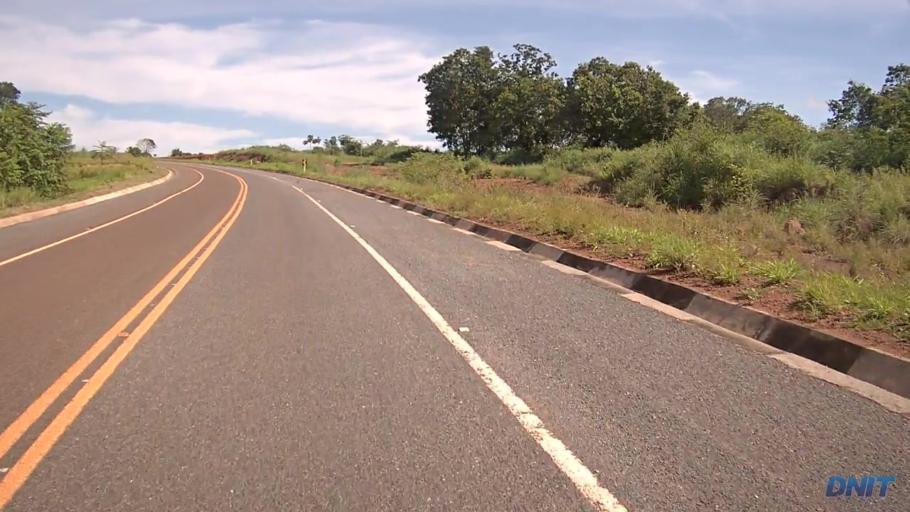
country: BR
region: Goias
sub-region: Sao Miguel Do Araguaia
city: Sao Miguel do Araguaia
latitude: -13.2905
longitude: -50.1779
